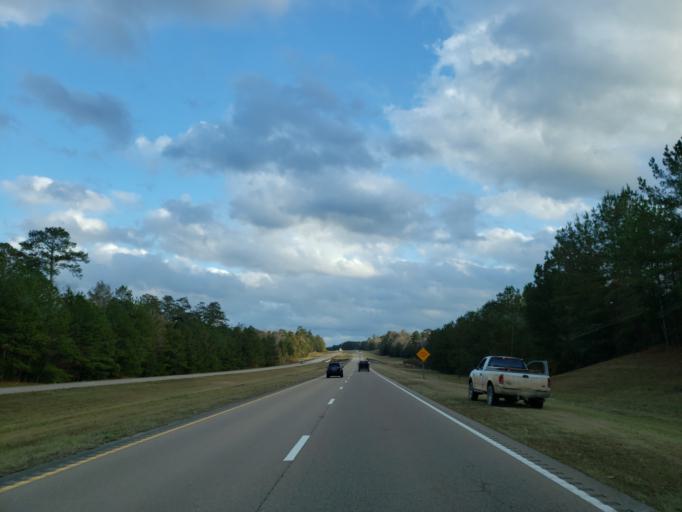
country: US
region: Mississippi
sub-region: Perry County
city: New Augusta
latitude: 31.1771
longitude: -88.9502
